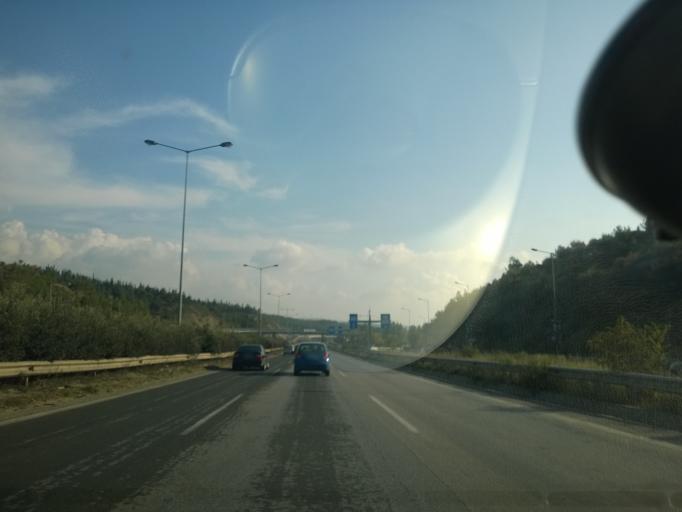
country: GR
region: Central Macedonia
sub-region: Nomos Thessalonikis
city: Triandria
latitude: 40.6279
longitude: 22.9773
